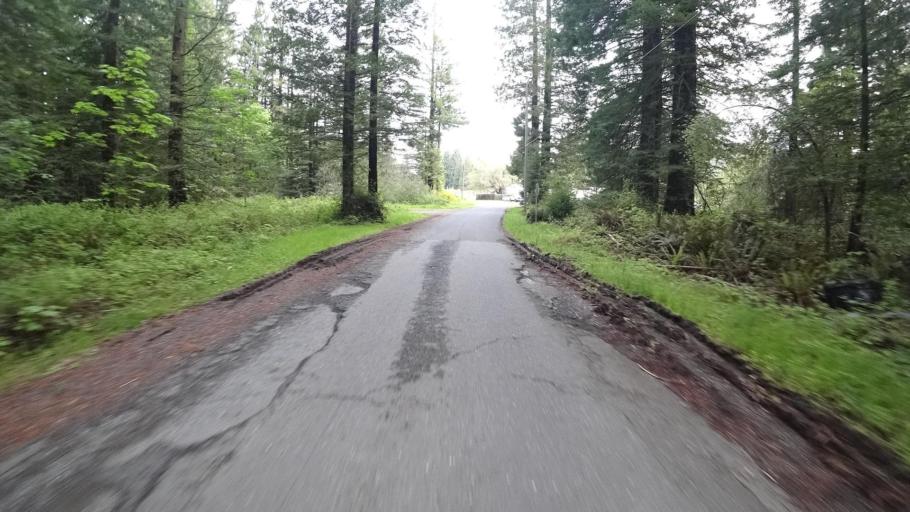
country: US
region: California
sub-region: Humboldt County
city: Redway
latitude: 40.3431
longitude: -123.9165
